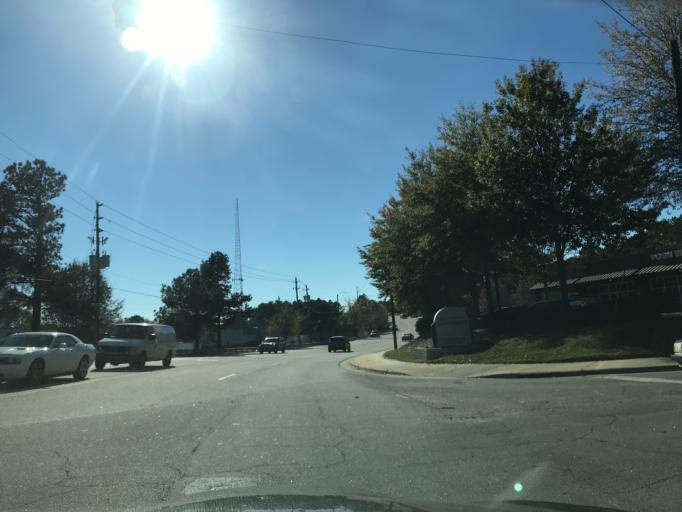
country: US
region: North Carolina
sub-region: Wake County
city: Raleigh
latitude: 35.8074
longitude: -78.6211
